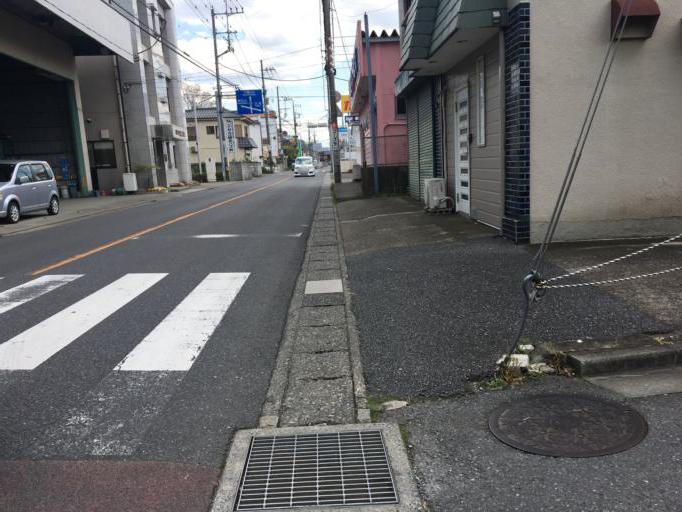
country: JP
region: Saitama
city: Kawagoe
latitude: 35.9285
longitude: 139.4765
